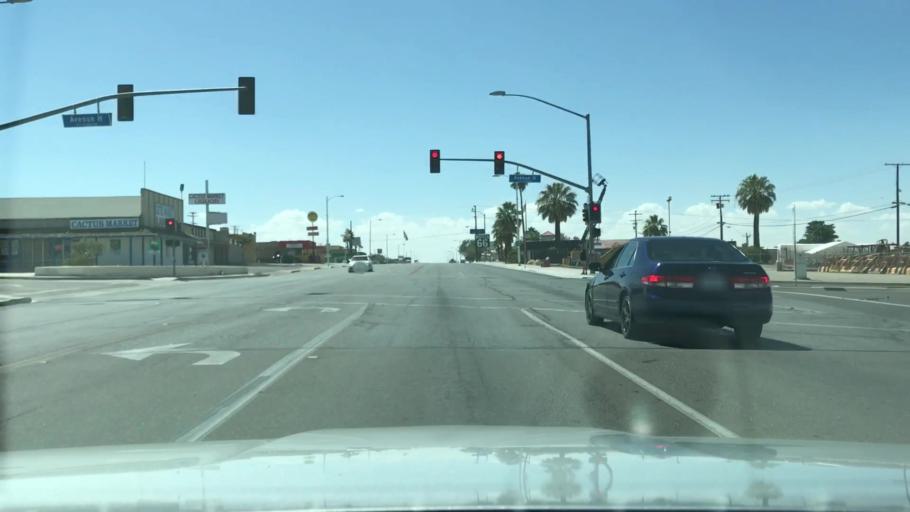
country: US
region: California
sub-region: San Bernardino County
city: Barstow
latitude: 34.8942
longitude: -117.0472
